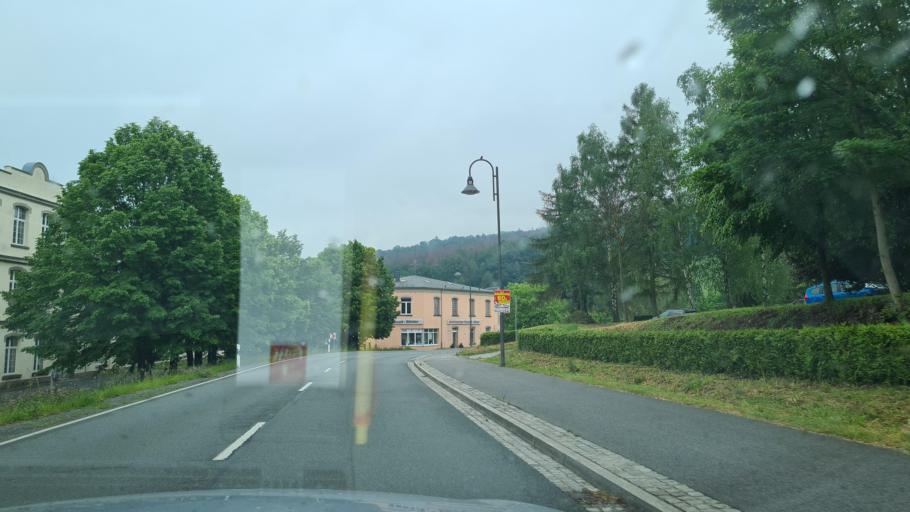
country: DE
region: Saxony
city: Schirgiswalde
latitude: 51.0795
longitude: 14.4317
